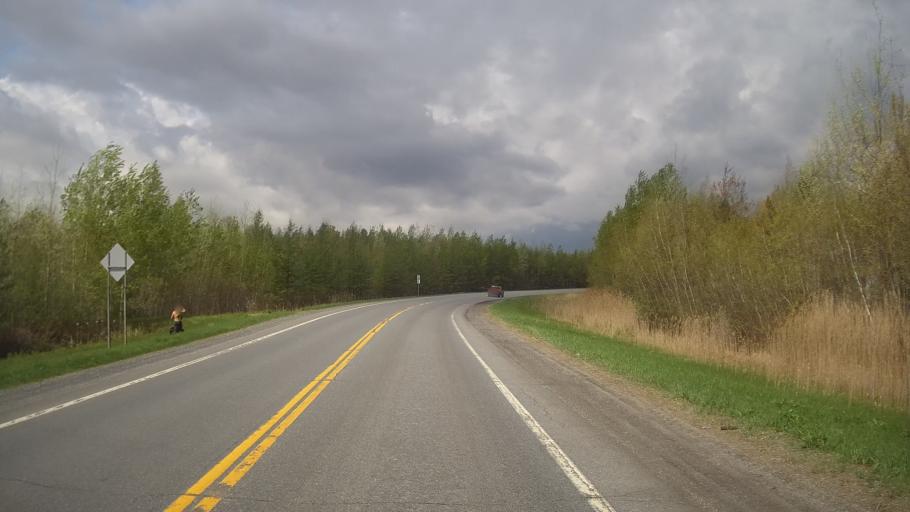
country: CA
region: Quebec
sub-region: Monteregie
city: Farnham
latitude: 45.2746
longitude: -72.9886
